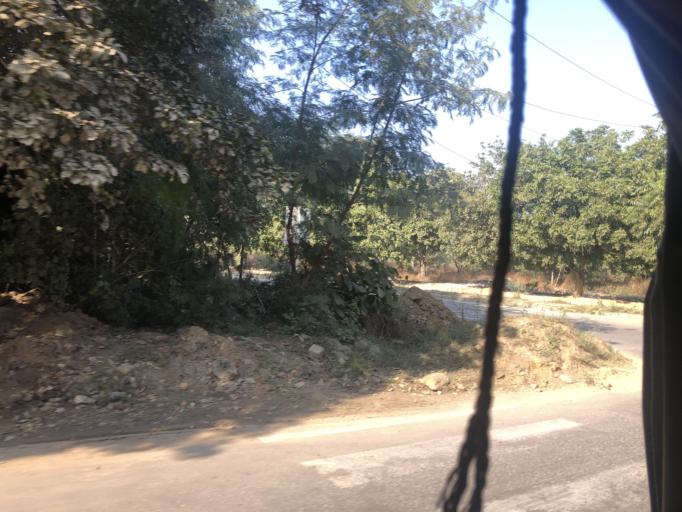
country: IN
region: Haryana
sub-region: Gurgaon
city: Gurgaon
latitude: 28.4621
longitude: 77.0688
